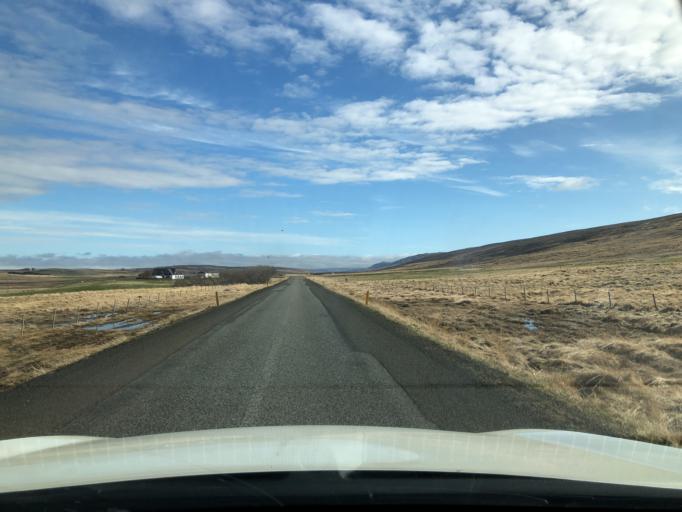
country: IS
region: West
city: Borgarnes
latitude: 65.0936
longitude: -21.7264
